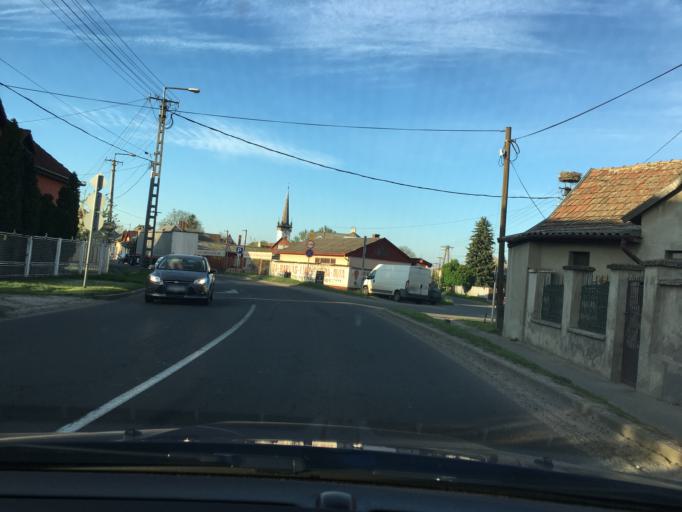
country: HU
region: Hajdu-Bihar
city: Mikepercs
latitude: 47.4380
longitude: 21.6311
